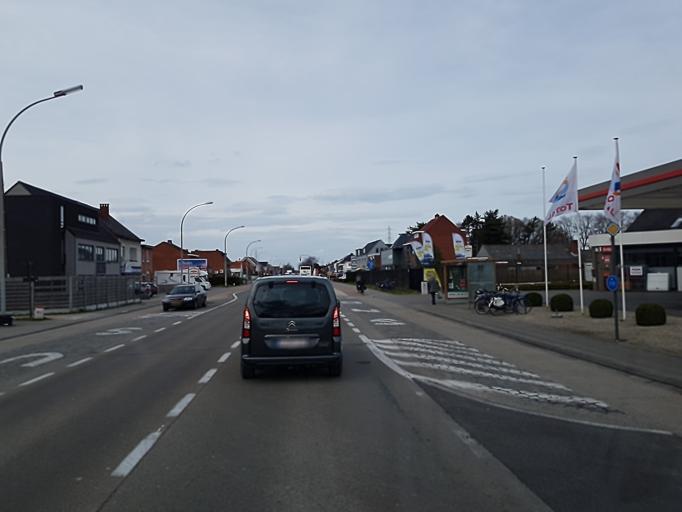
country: BE
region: Flanders
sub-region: Provincie Antwerpen
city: Mol
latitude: 51.2046
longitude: 5.1155
